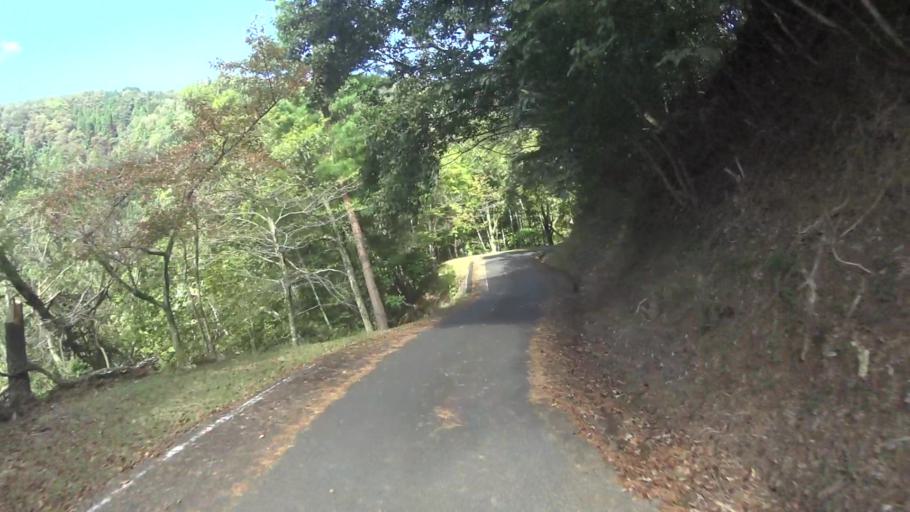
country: JP
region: Hyogo
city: Toyooka
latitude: 35.6099
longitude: 134.9926
